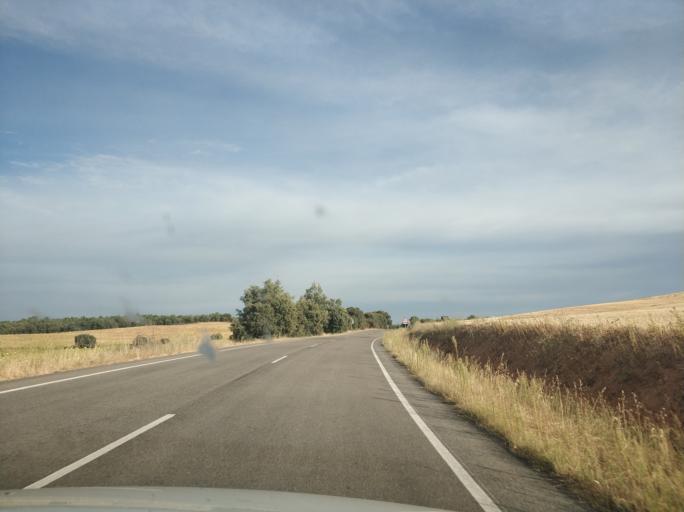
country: ES
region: Castille and Leon
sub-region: Provincia de Soria
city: Fuentearmegil
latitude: 41.6781
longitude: -3.2387
